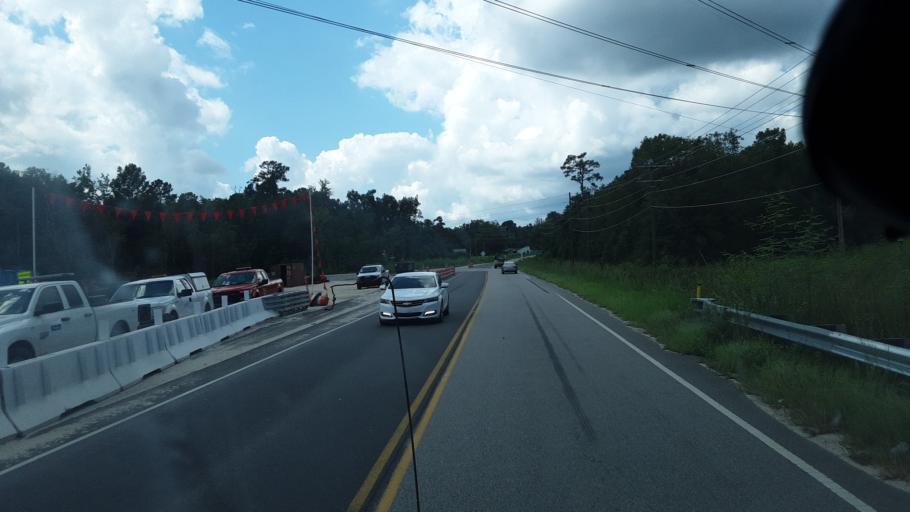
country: US
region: South Carolina
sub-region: Williamsburg County
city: Andrews
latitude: 33.3700
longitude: -79.4502
